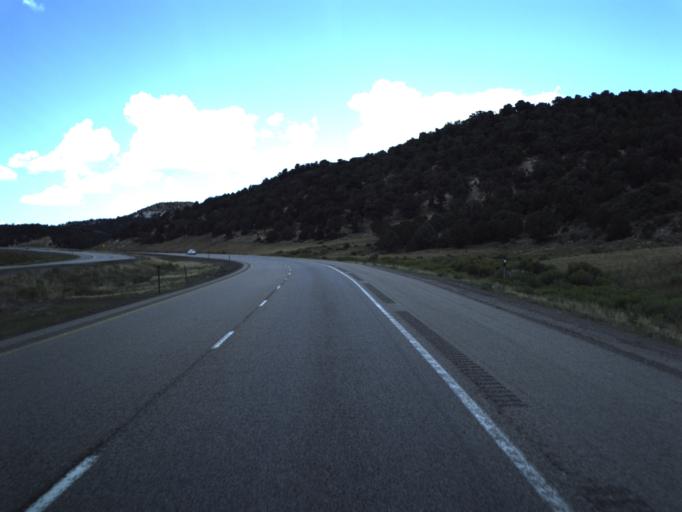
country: US
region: Utah
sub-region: Wayne County
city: Loa
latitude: 38.7715
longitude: -111.4730
